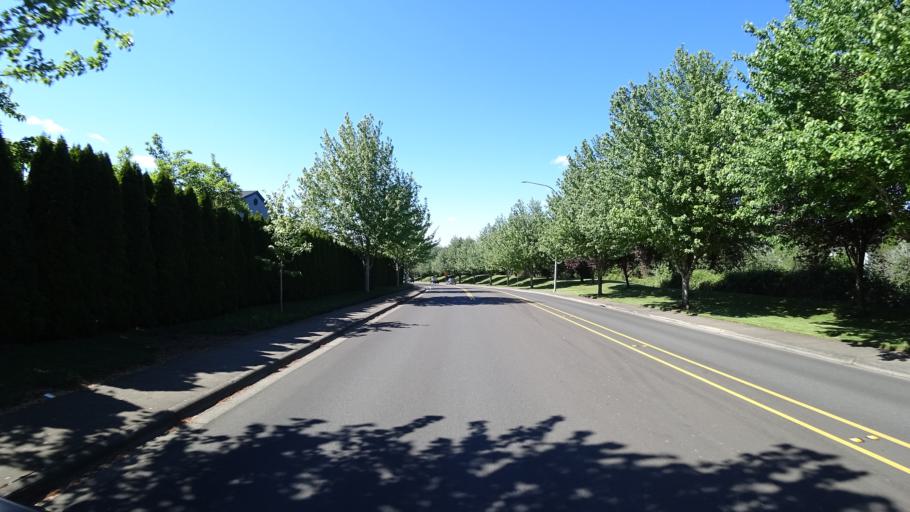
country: US
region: Oregon
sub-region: Washington County
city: Oak Hills
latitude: 45.5450
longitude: -122.8249
